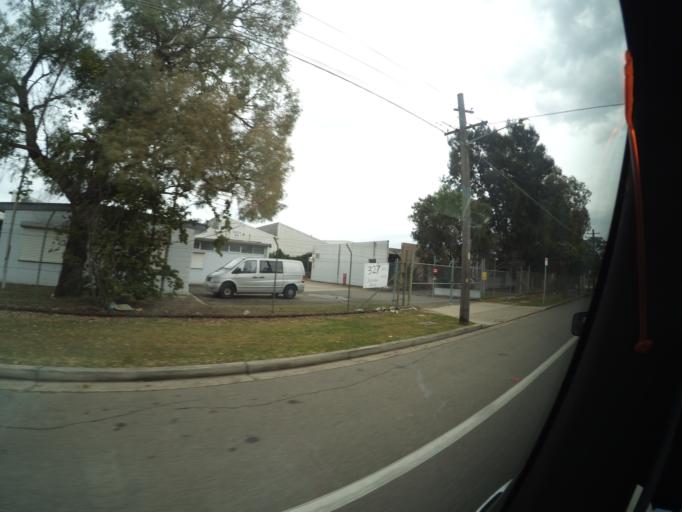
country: AU
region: New South Wales
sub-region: Bankstown
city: Regents Park
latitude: -33.8740
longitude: 151.0166
